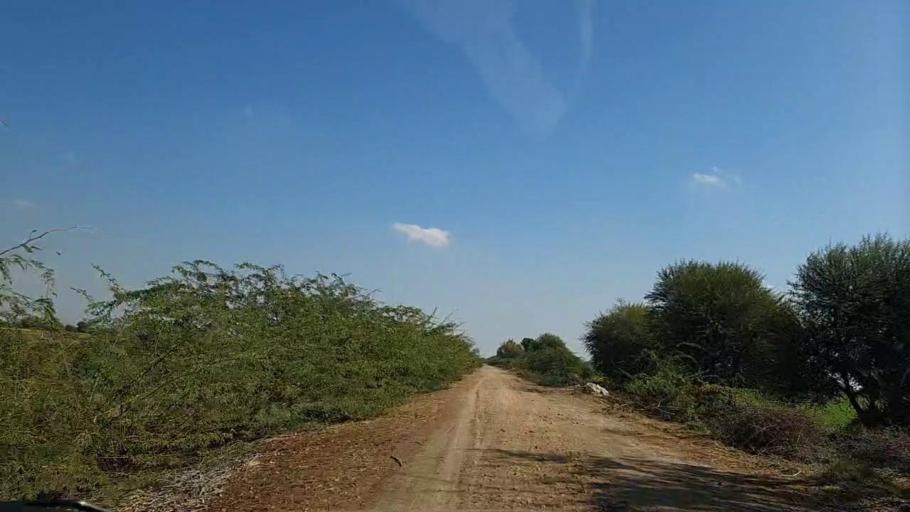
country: PK
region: Sindh
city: Pithoro
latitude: 25.6899
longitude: 69.3805
